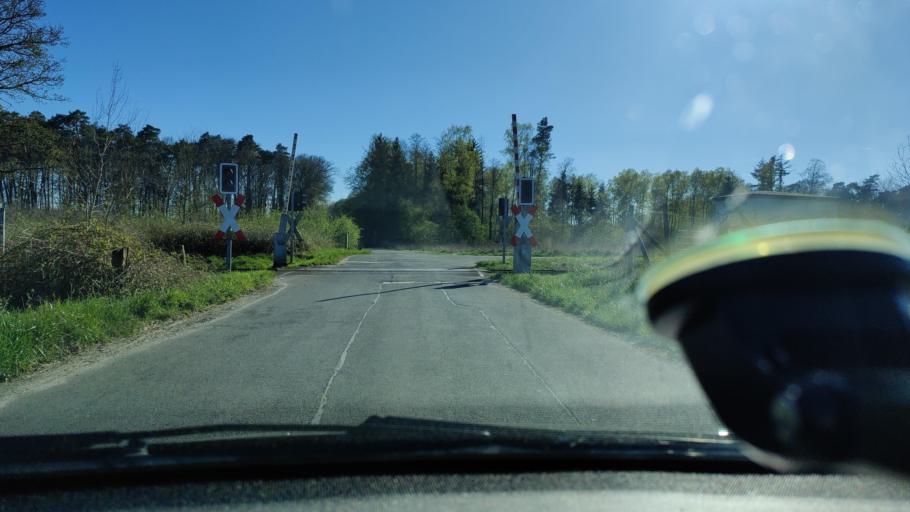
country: DE
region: North Rhine-Westphalia
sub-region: Regierungsbezirk Munster
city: Legden
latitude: 52.0461
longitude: 7.0648
